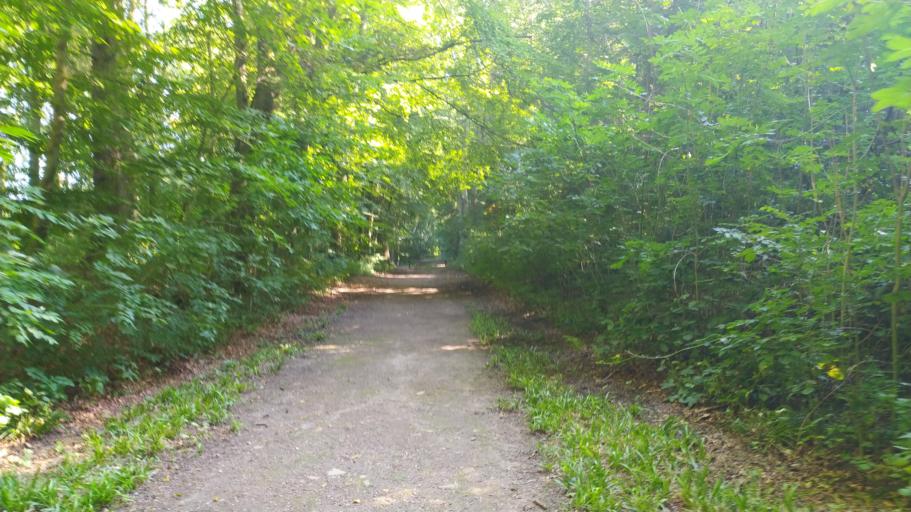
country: DE
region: Schleswig-Holstein
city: Kronshagen
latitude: 54.3650
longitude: 10.1014
